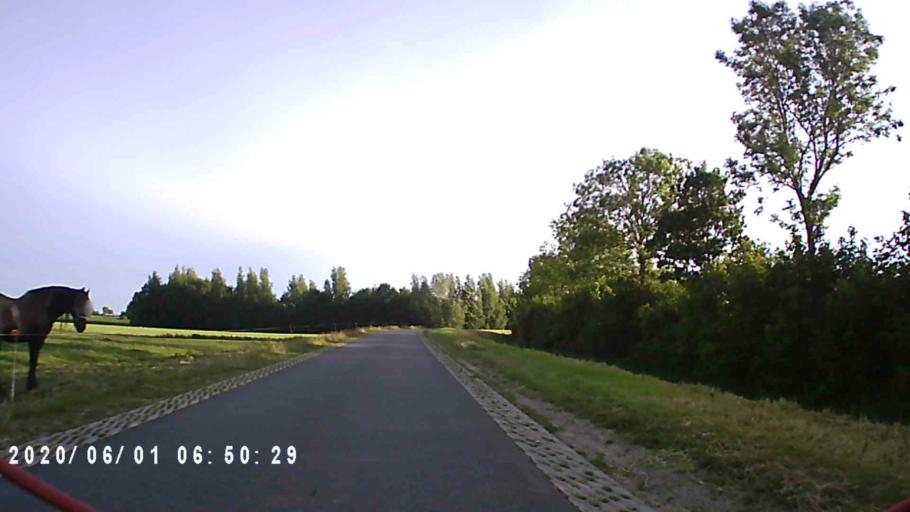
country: NL
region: Friesland
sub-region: Gemeente Kollumerland en Nieuwkruisland
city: Kollum
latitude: 53.3023
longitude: 6.1307
